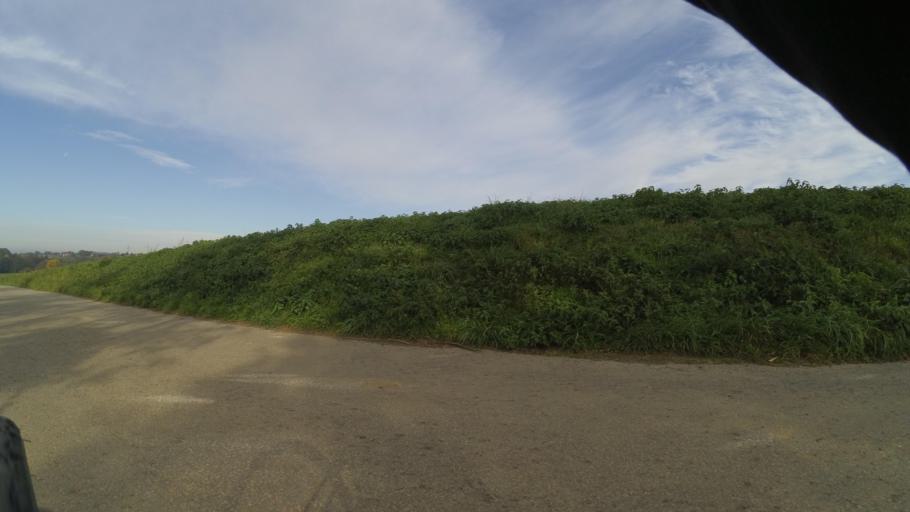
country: DE
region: Baden-Wuerttemberg
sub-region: Regierungsbezirk Stuttgart
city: Bretzfeld
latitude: 49.2122
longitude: 9.4479
